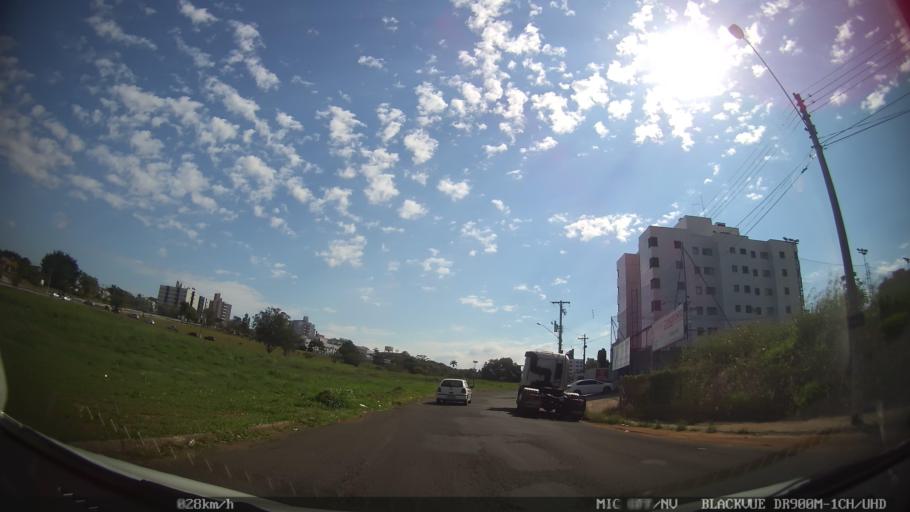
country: BR
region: Sao Paulo
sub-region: Americana
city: Americana
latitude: -22.7437
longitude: -47.3065
